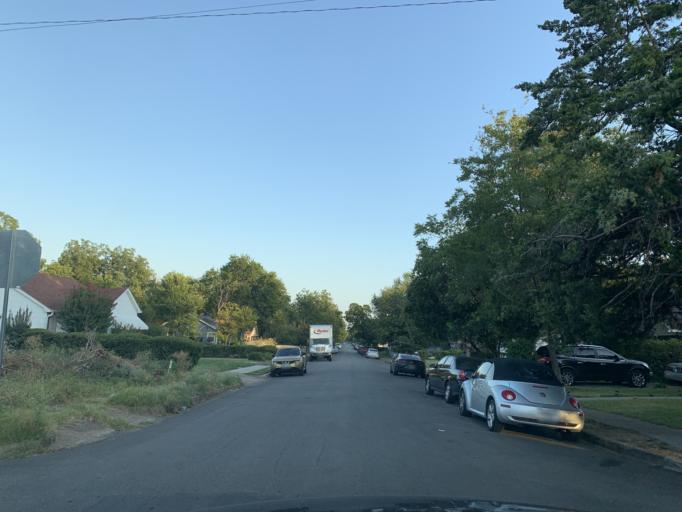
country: US
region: Texas
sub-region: Dallas County
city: Dallas
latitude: 32.7106
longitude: -96.8089
